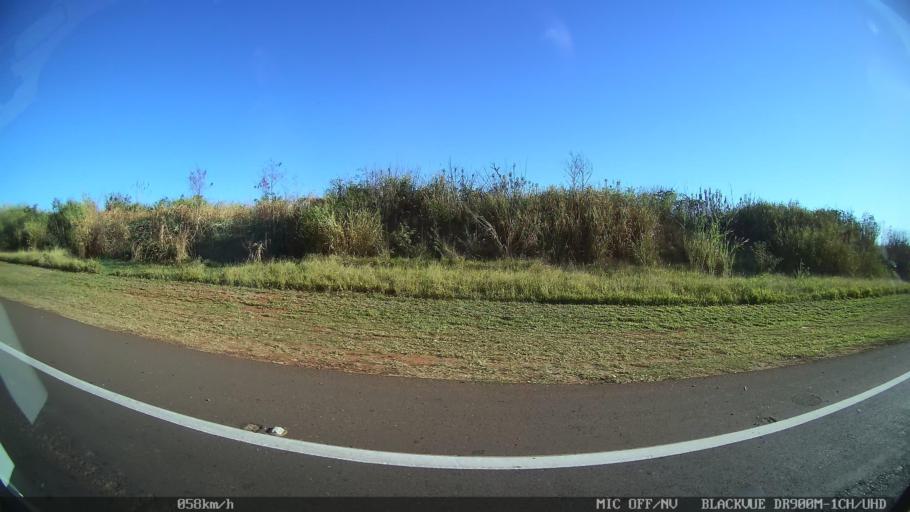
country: BR
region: Sao Paulo
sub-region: Americo Brasiliense
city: Americo Brasiliense
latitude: -21.7592
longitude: -48.1179
